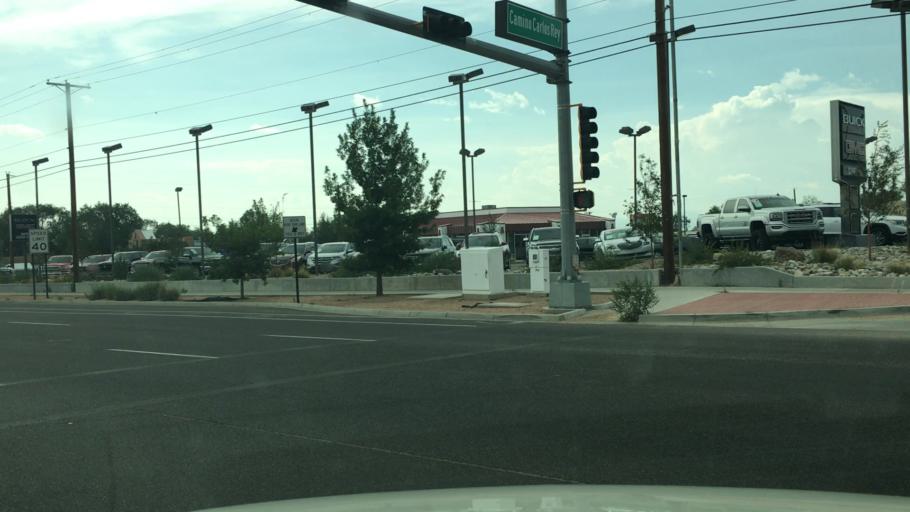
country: US
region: New Mexico
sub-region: Santa Fe County
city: Agua Fria
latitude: 35.6581
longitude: -105.9863
